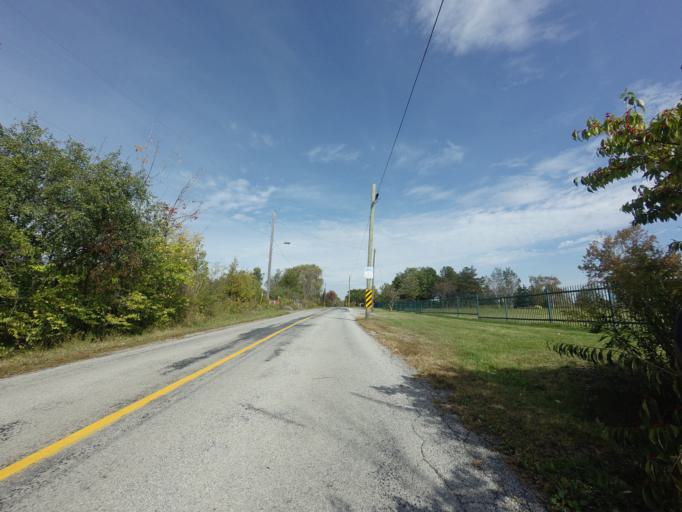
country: CA
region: Ontario
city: Hamilton
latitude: 43.3087
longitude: -79.8959
